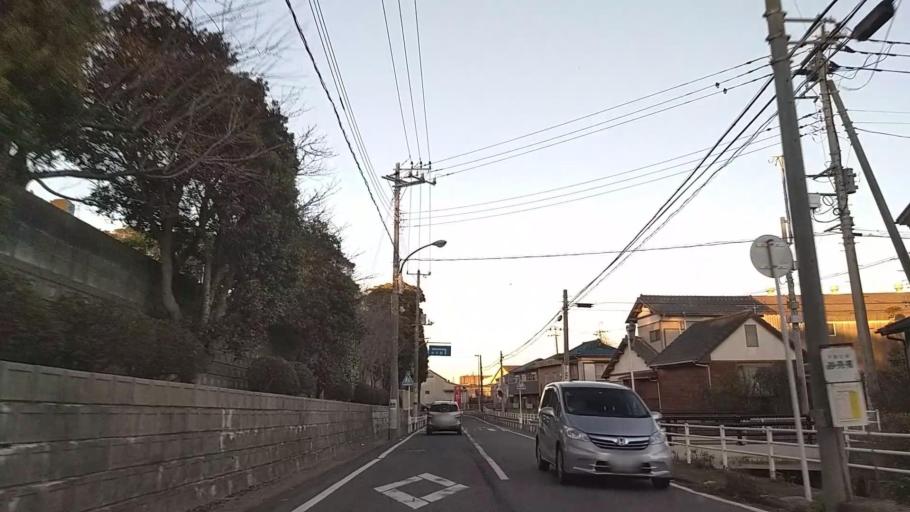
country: JP
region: Chiba
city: Hasaki
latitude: 35.7270
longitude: 140.8310
